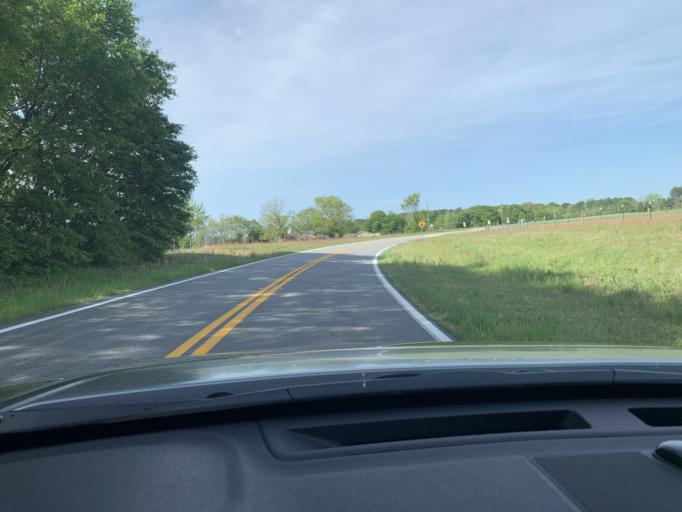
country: US
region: Georgia
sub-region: Oconee County
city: Watkinsville
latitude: 33.8126
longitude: -83.3991
